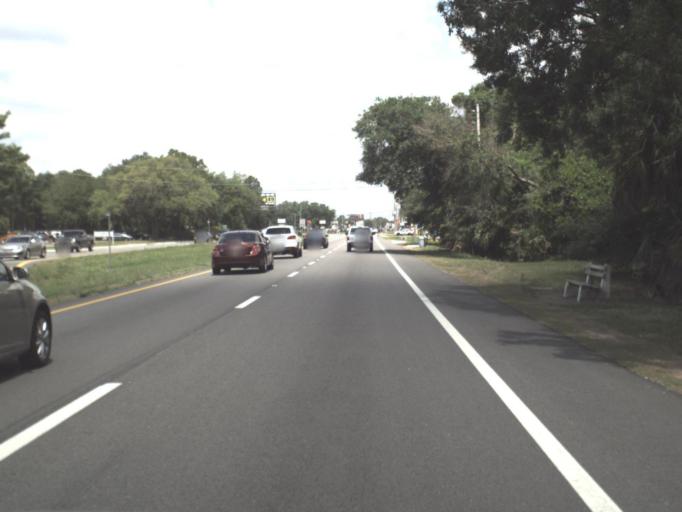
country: US
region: Florida
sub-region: Saint Johns County
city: Fruit Cove
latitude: 30.2066
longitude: -81.5771
